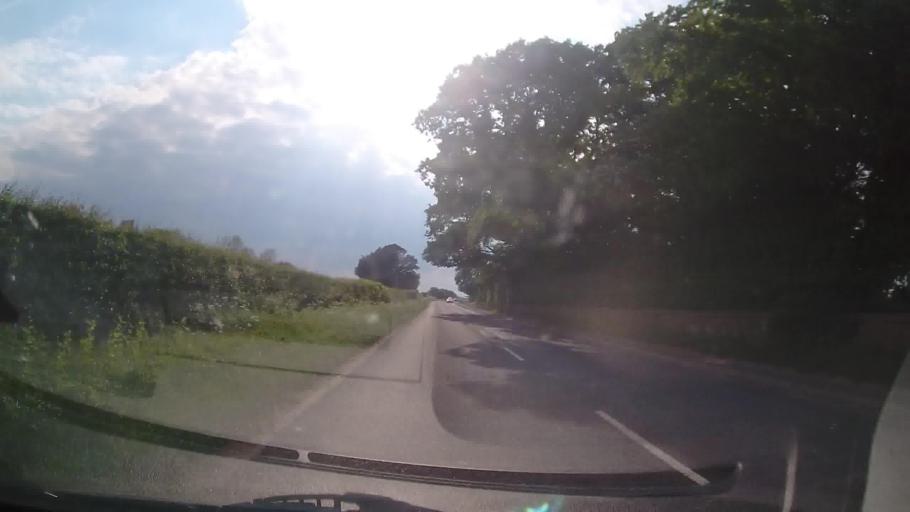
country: GB
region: England
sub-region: Telford and Wrekin
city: Wellington
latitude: 52.6924
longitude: -2.5453
